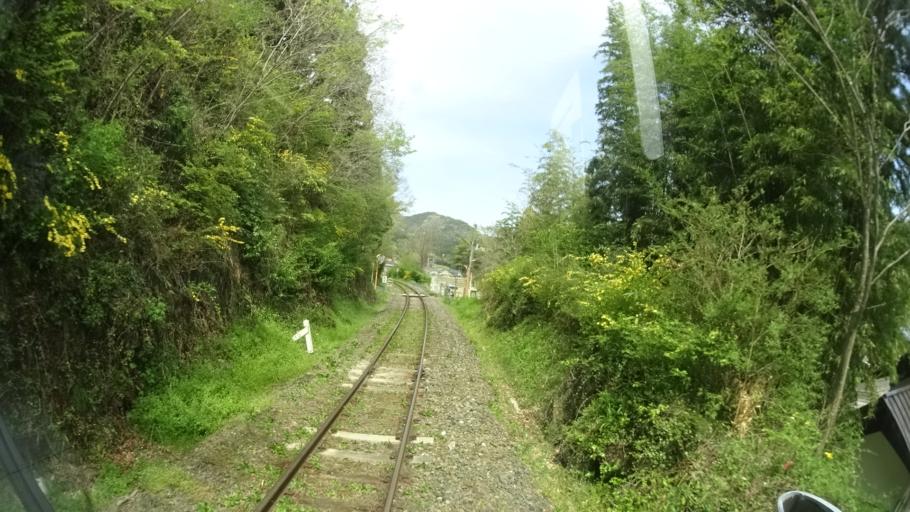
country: JP
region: Iwate
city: Ichinoseki
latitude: 38.9600
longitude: 141.2439
